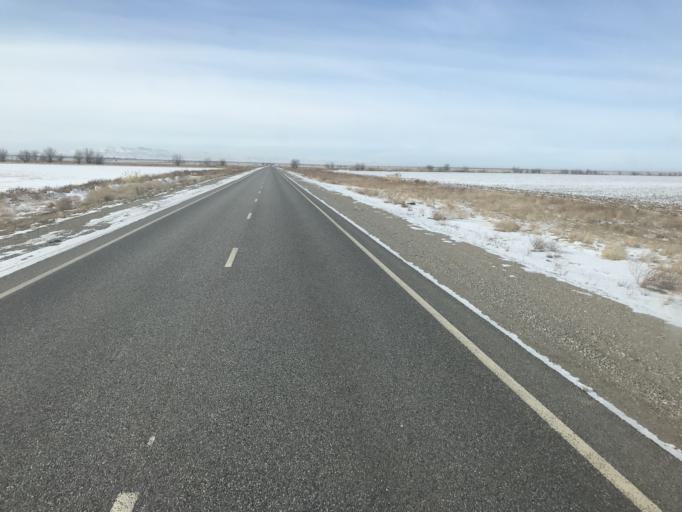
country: KZ
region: Zhambyl
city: Taraz
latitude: 43.0288
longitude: 71.3708
